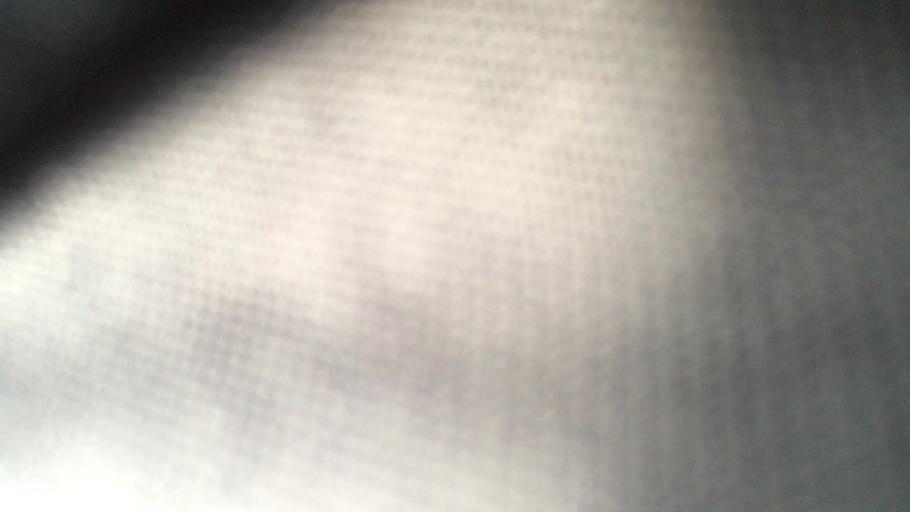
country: US
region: Maryland
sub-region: Somerset County
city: Princess Anne
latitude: 38.1623
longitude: -75.6895
